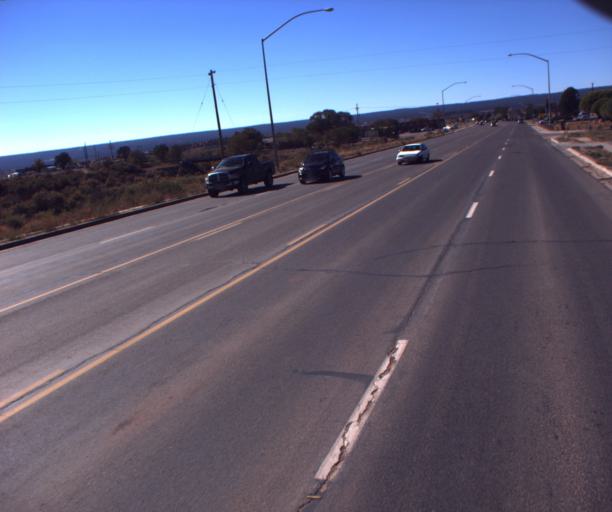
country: US
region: Arizona
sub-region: Apache County
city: Window Rock
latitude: 35.6633
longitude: -109.0522
